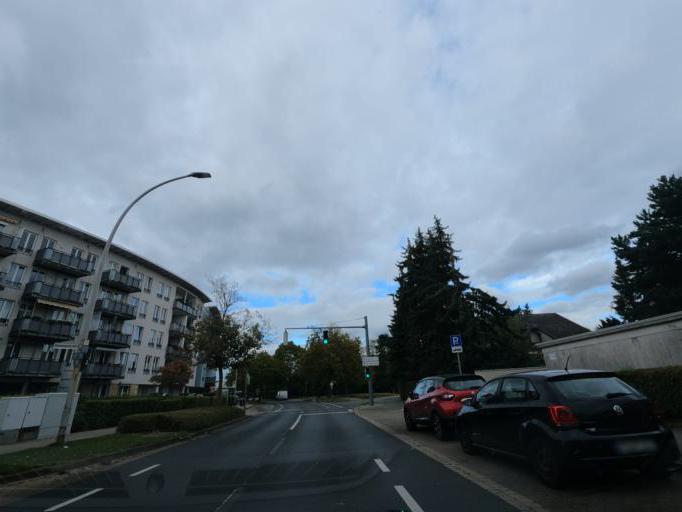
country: DE
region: Lower Saxony
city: Leiferde
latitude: 52.2451
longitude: 10.4815
